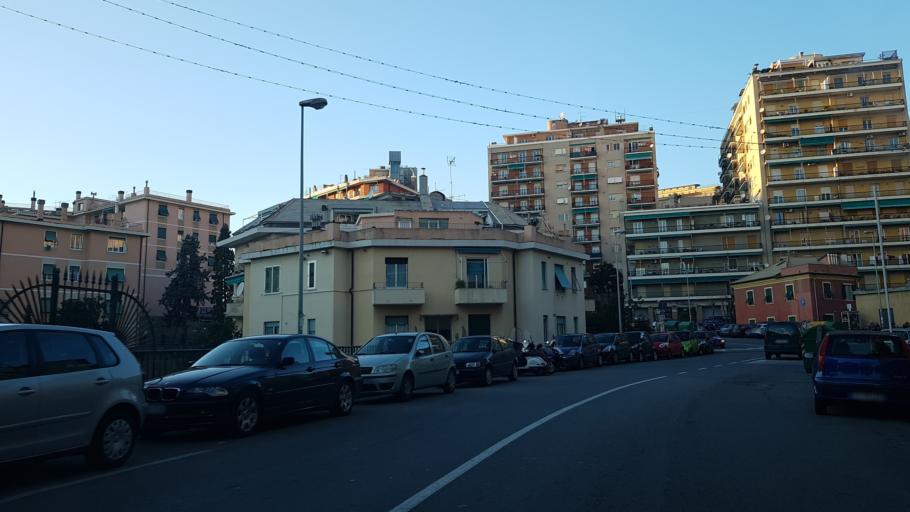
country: IT
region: Liguria
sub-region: Provincia di Genova
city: Genoa
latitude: 44.4079
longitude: 8.9790
